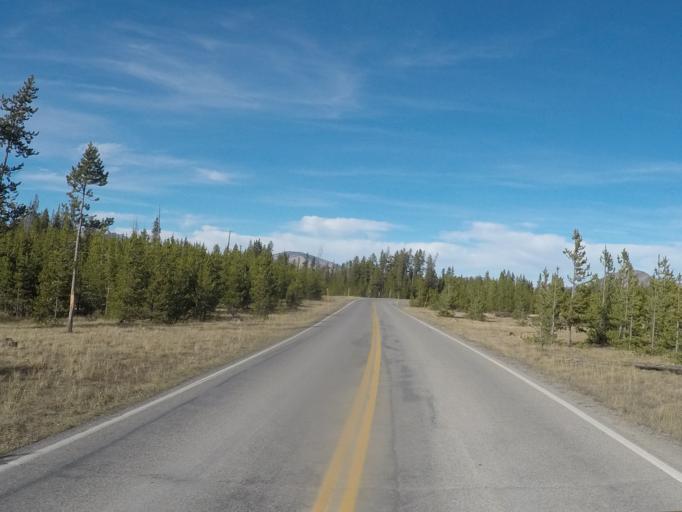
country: US
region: Montana
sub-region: Gallatin County
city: West Yellowstone
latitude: 44.8758
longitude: -110.7367
